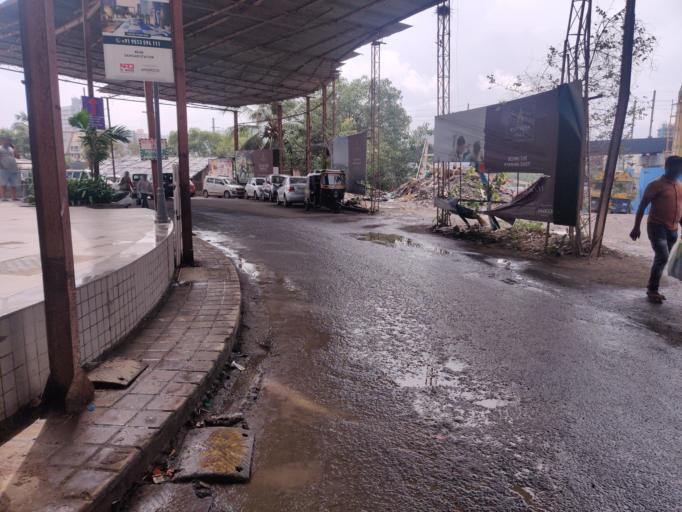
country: IN
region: Maharashtra
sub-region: Mumbai Suburban
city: Borivli
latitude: 19.2484
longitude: 72.8642
